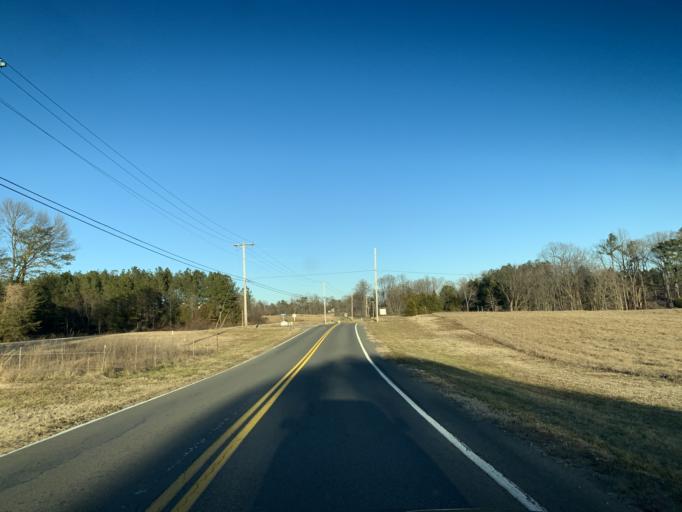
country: US
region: Maryland
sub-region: Saint Mary's County
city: Mechanicsville
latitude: 38.4458
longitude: -76.7257
